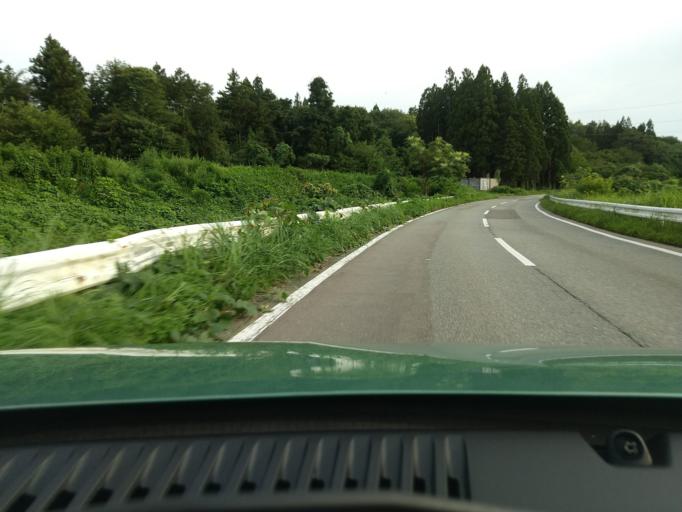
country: JP
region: Akita
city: Akita
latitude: 39.7580
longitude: 140.1610
